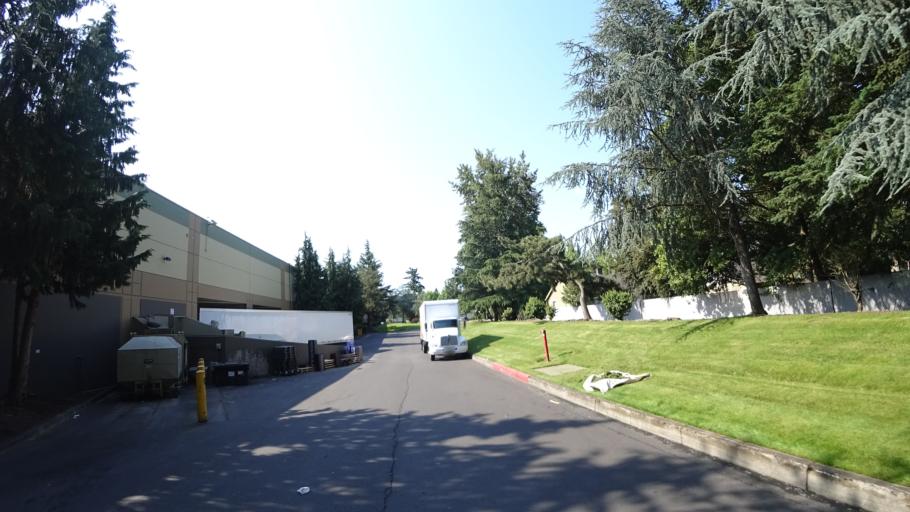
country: US
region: Oregon
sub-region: Multnomah County
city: Lents
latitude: 45.4591
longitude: -122.5821
